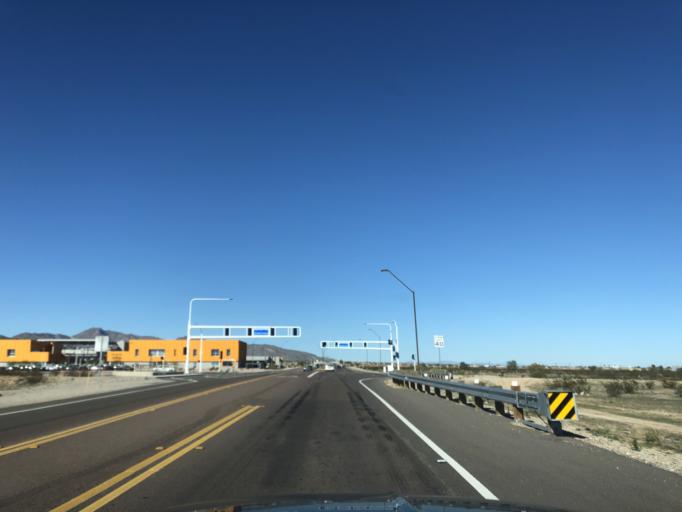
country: US
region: Arizona
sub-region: Maricopa County
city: Buckeye
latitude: 33.4491
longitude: -112.5043
